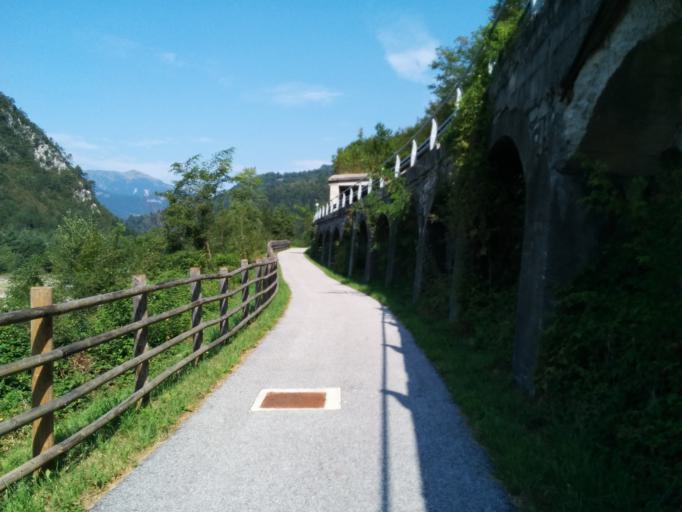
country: IT
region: Friuli Venezia Giulia
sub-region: Provincia di Udine
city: Villa Santina
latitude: 46.4227
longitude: 12.9060
